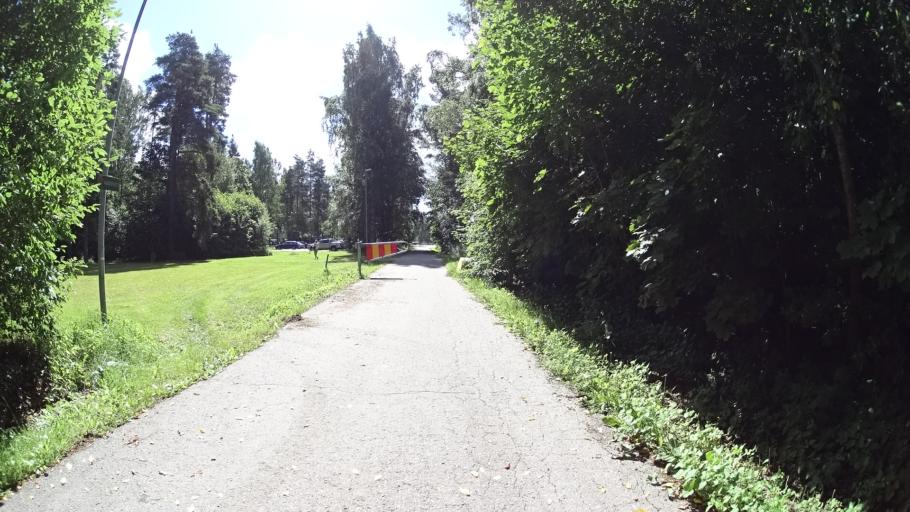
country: FI
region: Uusimaa
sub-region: Helsinki
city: Tuusula
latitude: 60.3917
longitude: 25.0250
